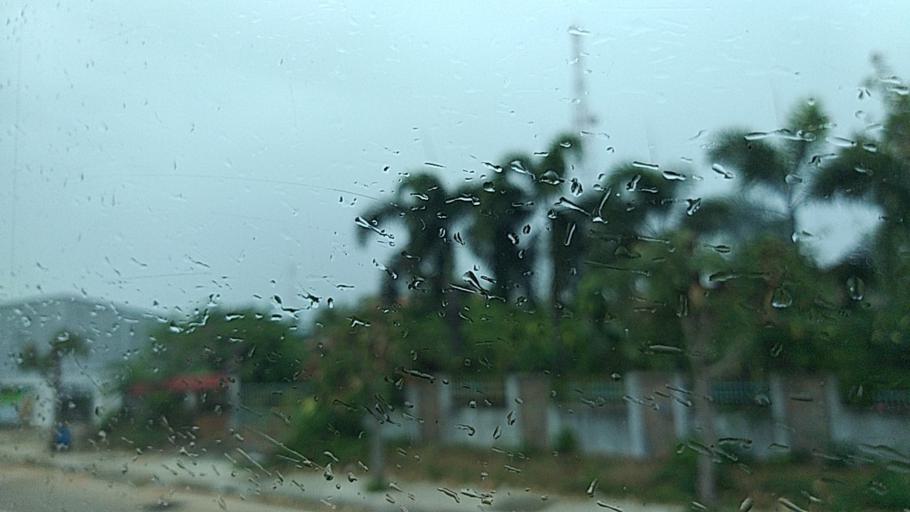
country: TH
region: Maha Sarakham
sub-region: Amphoe Borabue
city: Borabue
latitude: 16.0378
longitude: 103.1228
